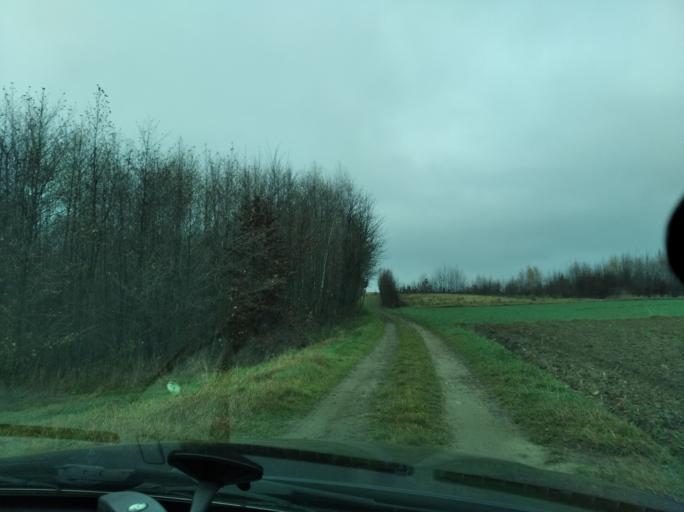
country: PL
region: Subcarpathian Voivodeship
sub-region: Powiat przeworski
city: Jawornik Polski
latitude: 49.8942
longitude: 22.2752
